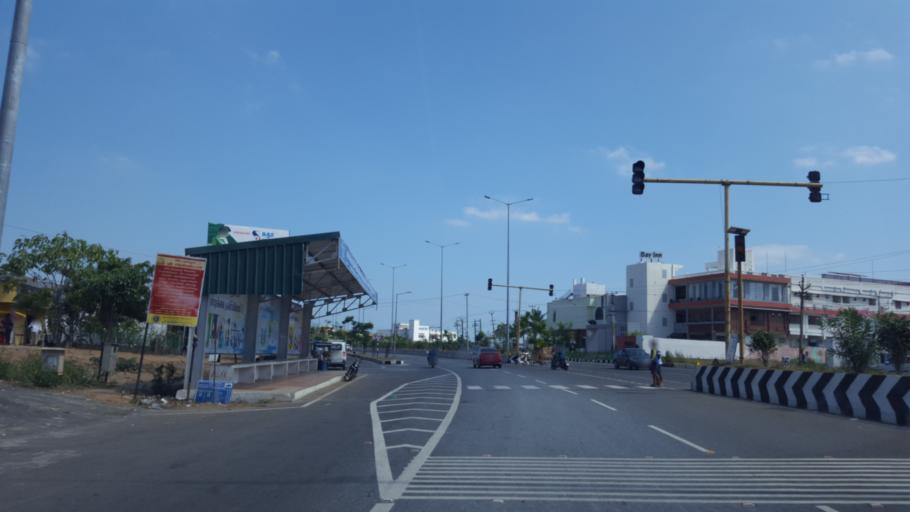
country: IN
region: Tamil Nadu
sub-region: Kancheepuram
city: Mamallapuram
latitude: 12.6281
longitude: 80.1945
